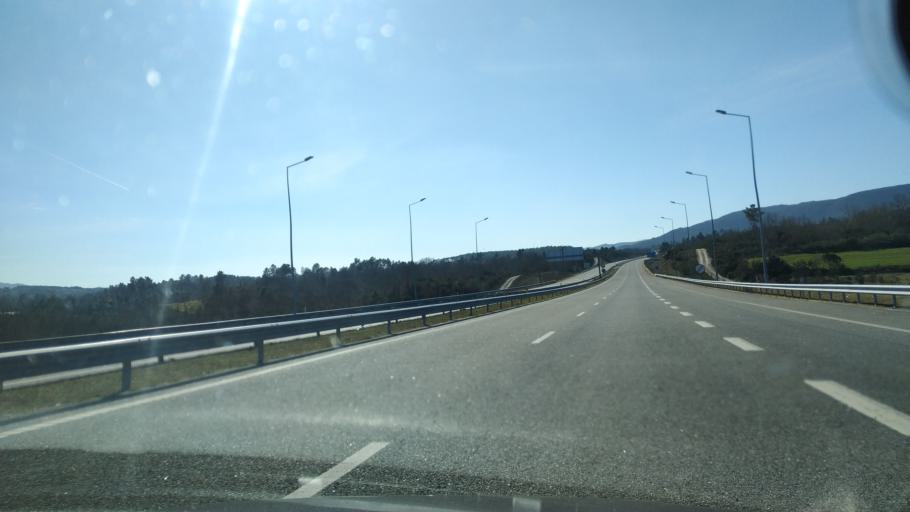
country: PT
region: Vila Real
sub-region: Chaves
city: Chaves
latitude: 41.7654
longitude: -7.4965
